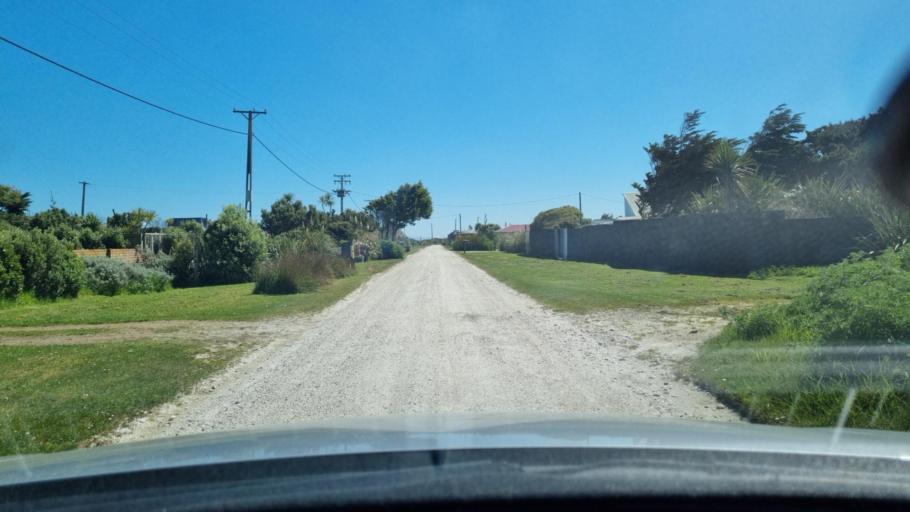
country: NZ
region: Southland
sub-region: Invercargill City
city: Invercargill
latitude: -46.4311
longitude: 168.2333
